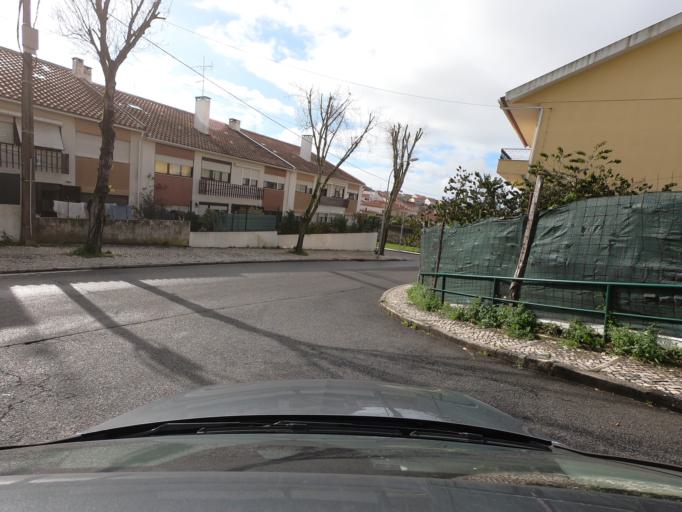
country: PT
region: Lisbon
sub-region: Oeiras
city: Porto Salvo
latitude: 38.7255
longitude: -9.3100
